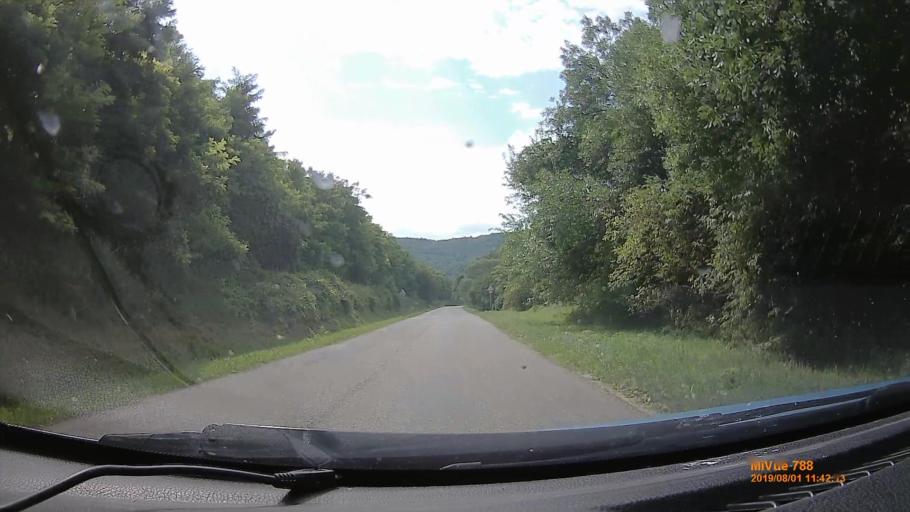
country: HU
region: Baranya
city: Villany
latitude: 45.8872
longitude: 18.4114
